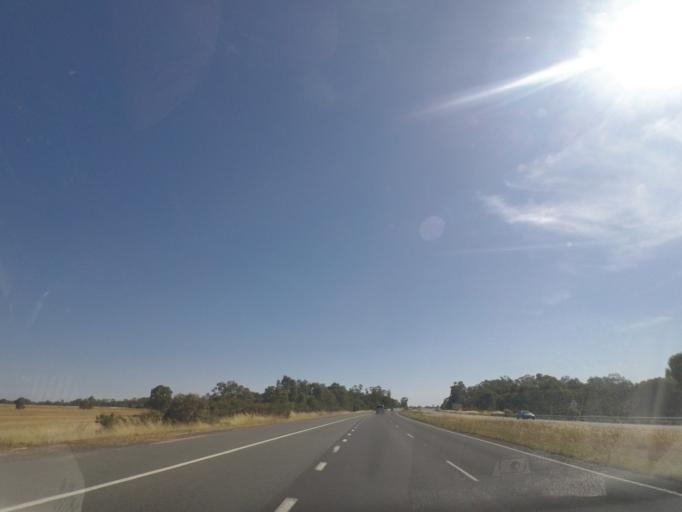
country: AU
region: Victoria
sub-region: Greater Shepparton
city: Shepparton
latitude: -36.6164
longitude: 145.3114
